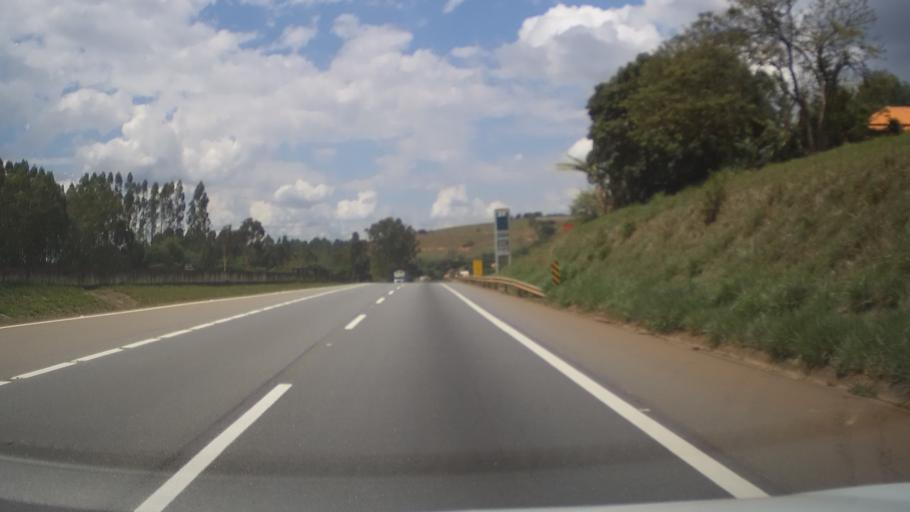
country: BR
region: Minas Gerais
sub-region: Nepomuceno
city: Nepomuceno
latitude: -21.3029
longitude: -45.1545
